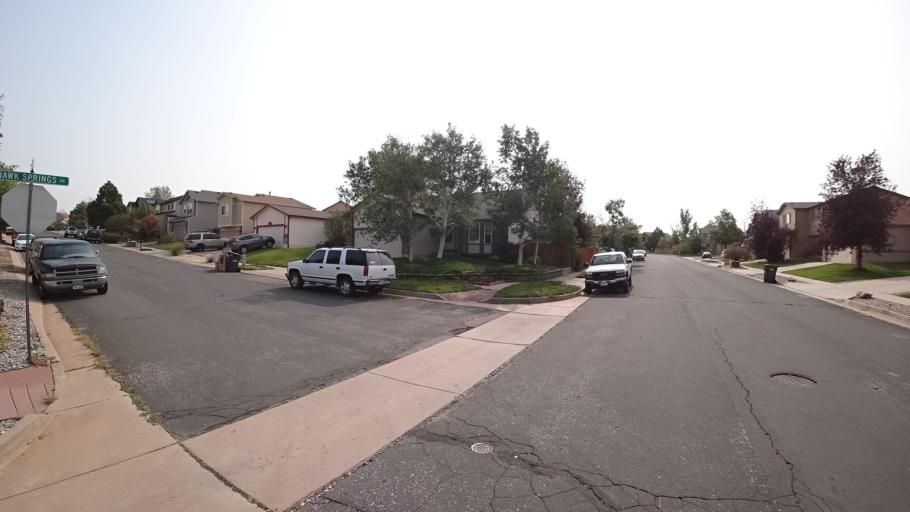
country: US
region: Colorado
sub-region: El Paso County
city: Cimarron Hills
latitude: 38.9271
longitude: -104.7323
